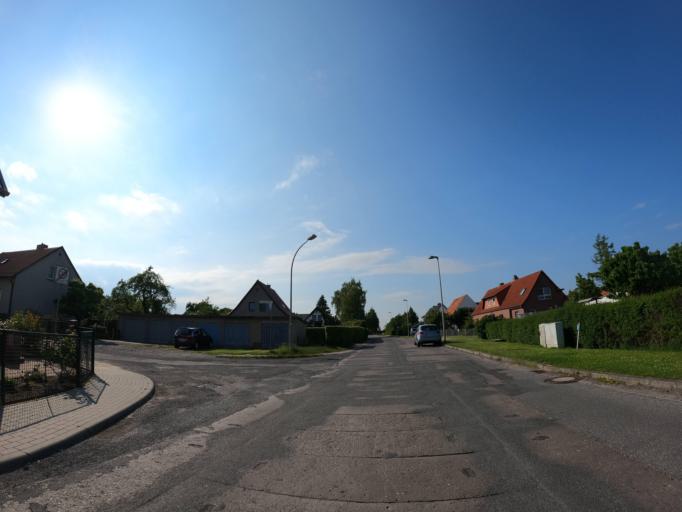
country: DE
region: Mecklenburg-Vorpommern
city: Stralsund
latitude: 54.2953
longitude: 13.0664
